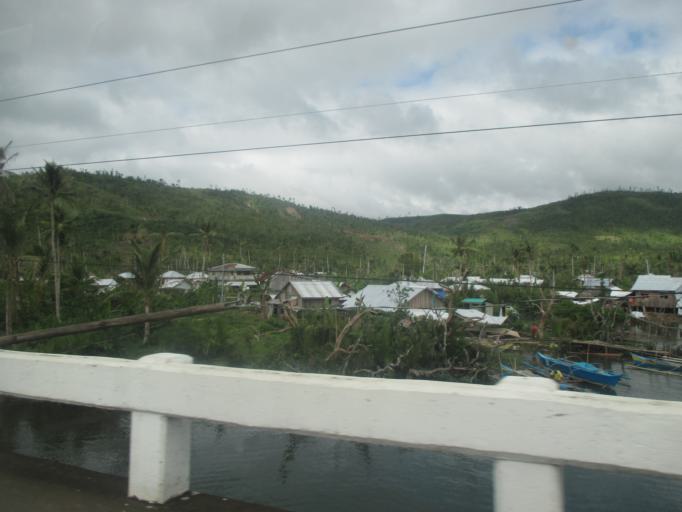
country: PH
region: Eastern Visayas
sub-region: Province of Eastern Samar
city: Lawa-an
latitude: 11.1295
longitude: 125.2595
